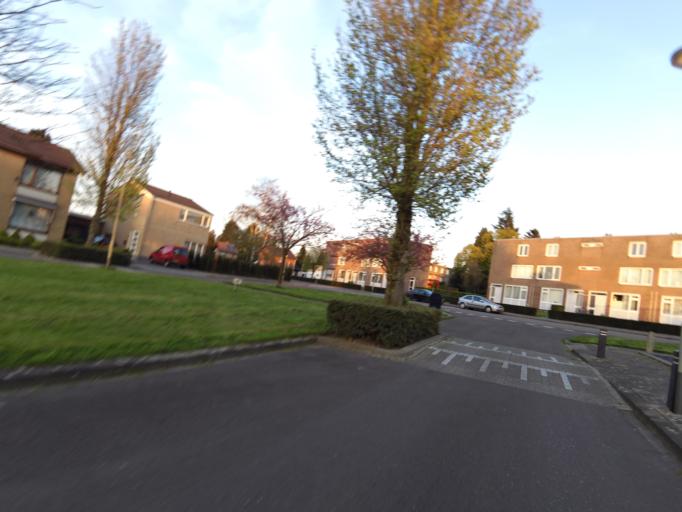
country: NL
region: Limburg
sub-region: Gemeente Kerkrade
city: Kerkrade
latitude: 50.9042
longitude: 6.0311
